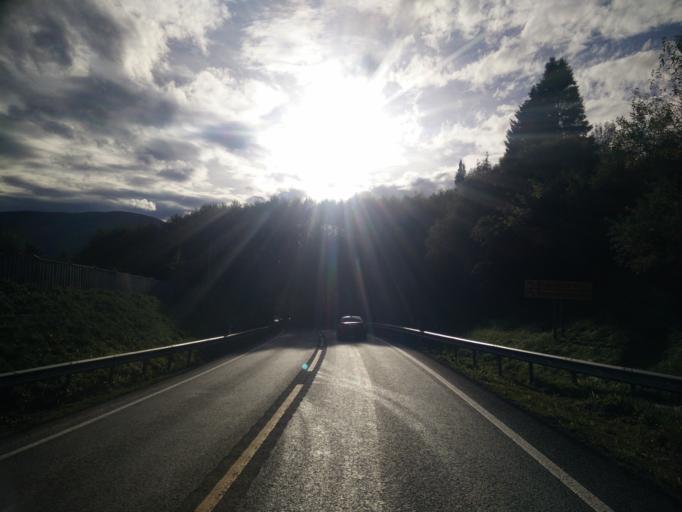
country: NO
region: More og Romsdal
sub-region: Vestnes
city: Vestnes
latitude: 62.6117
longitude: 7.0917
